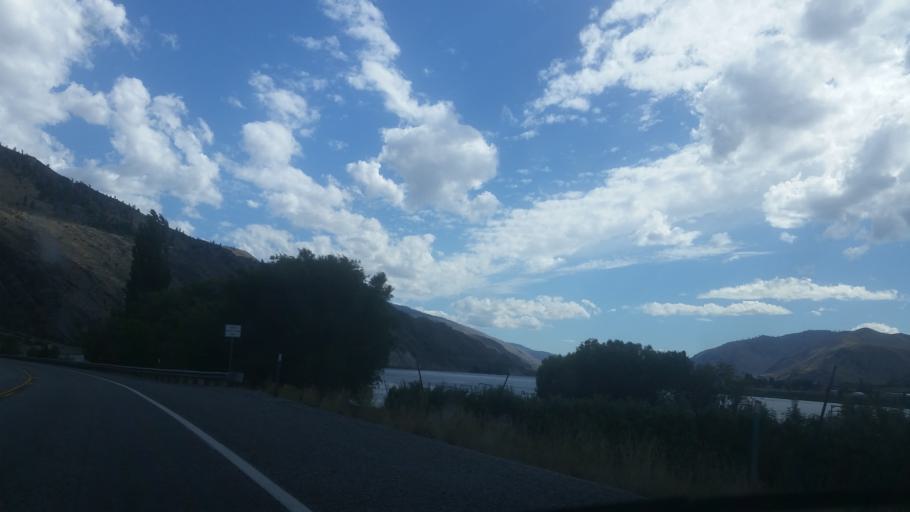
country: US
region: Washington
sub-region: Chelan County
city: Entiat
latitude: 47.6997
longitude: -120.1937
